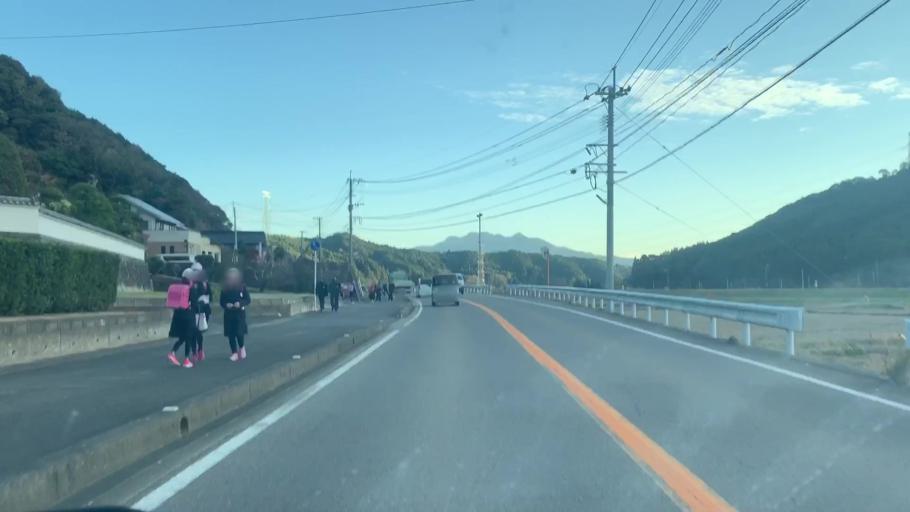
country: JP
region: Saga Prefecture
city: Karatsu
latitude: 33.3674
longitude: 130.0052
